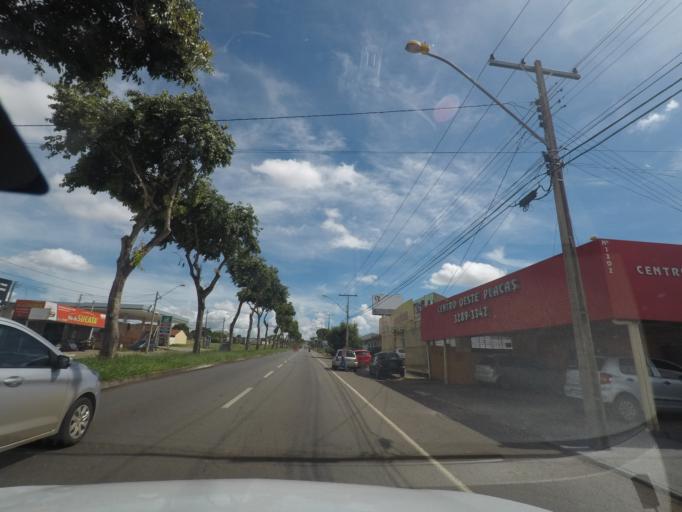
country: BR
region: Goias
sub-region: Goiania
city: Goiania
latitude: -16.7398
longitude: -49.3283
